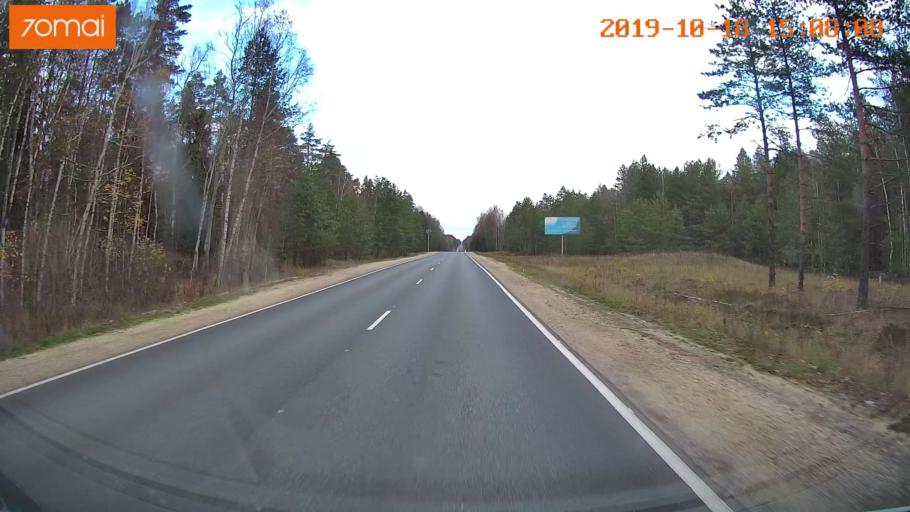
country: RU
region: Vladimir
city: Gus'-Khrustal'nyy
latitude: 55.5481
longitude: 40.6073
